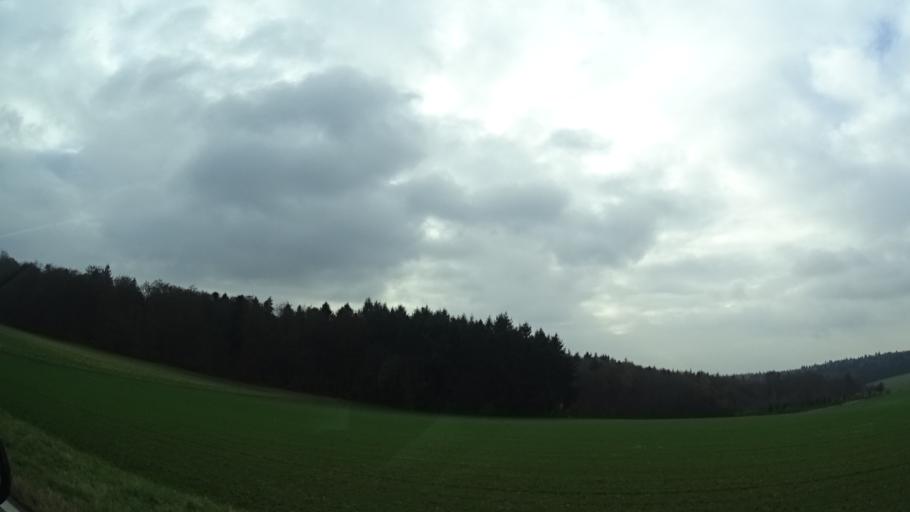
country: DE
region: Baden-Wuerttemberg
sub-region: Karlsruhe Region
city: Neunkirchen
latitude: 49.4009
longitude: 8.9822
